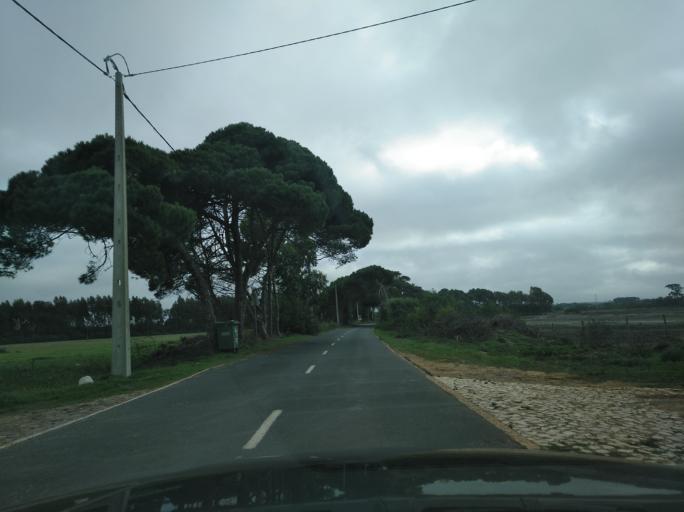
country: PT
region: Beja
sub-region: Odemira
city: Vila Nova de Milfontes
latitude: 37.7059
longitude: -8.7732
